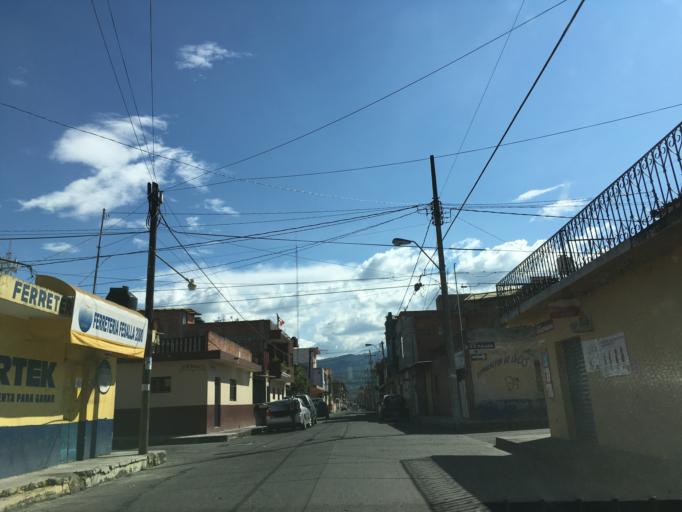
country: MX
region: Michoacan
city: Zacapu
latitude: 19.8188
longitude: -101.7841
